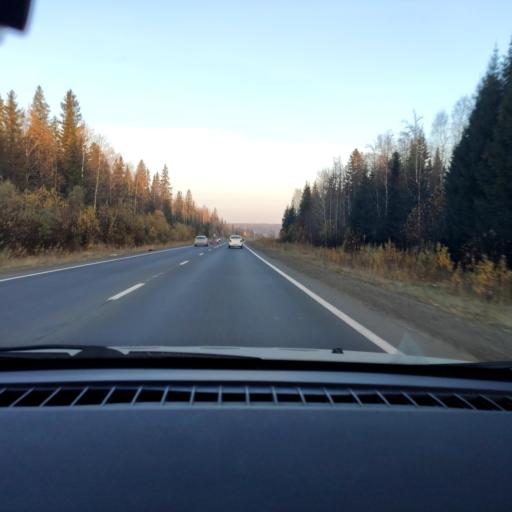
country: RU
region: Perm
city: Novyye Lyady
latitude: 58.0312
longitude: 56.4855
